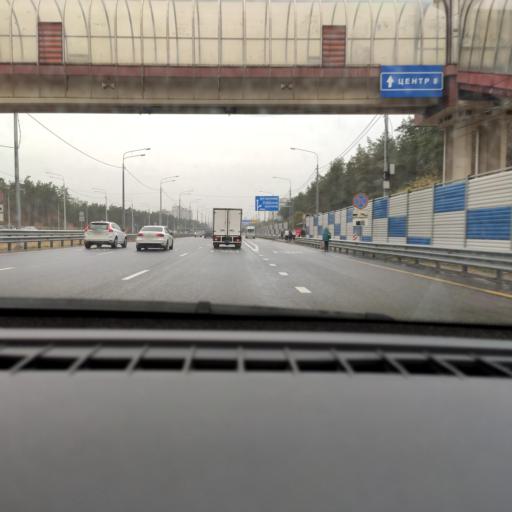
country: RU
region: Voronezj
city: Podgornoye
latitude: 51.7402
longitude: 39.1834
